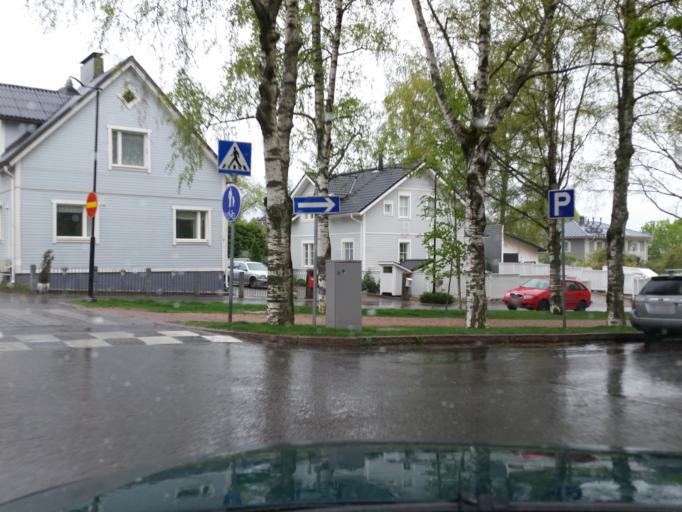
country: FI
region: Uusimaa
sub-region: Helsinki
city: Lohja
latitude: 60.2500
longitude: 24.0587
